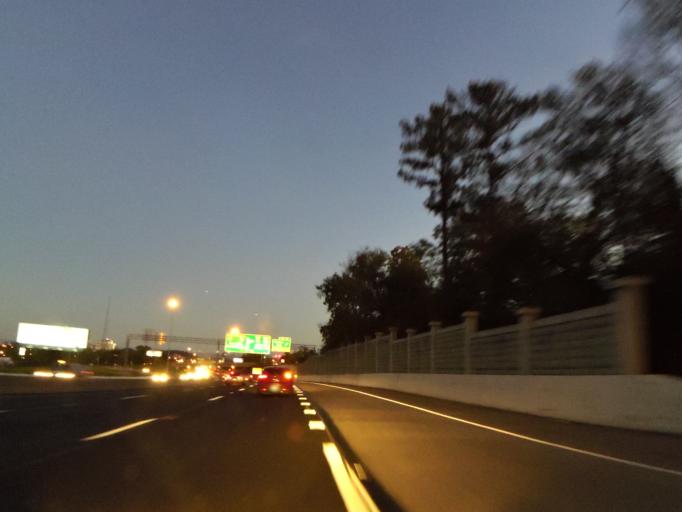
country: US
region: Tennessee
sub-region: Knox County
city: Knoxville
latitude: 35.9795
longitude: -83.9371
